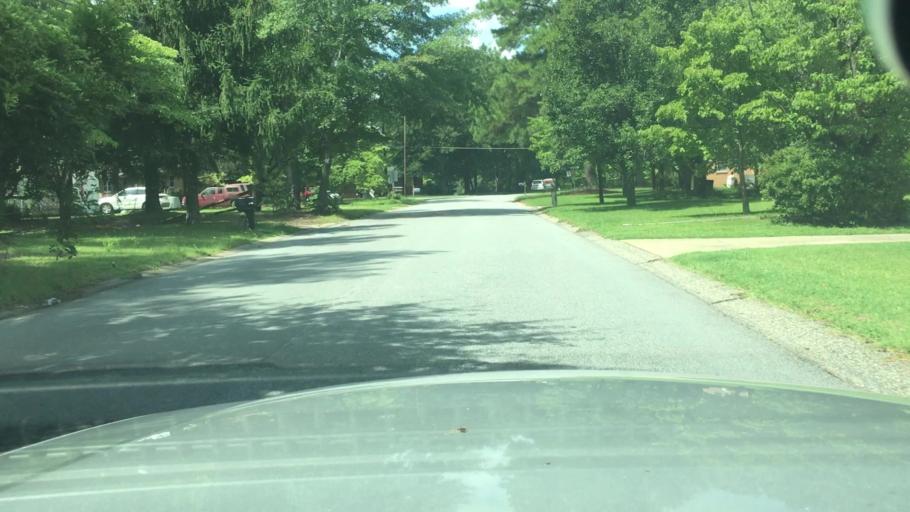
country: US
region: North Carolina
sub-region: Cumberland County
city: Hope Mills
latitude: 35.0325
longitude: -78.9891
